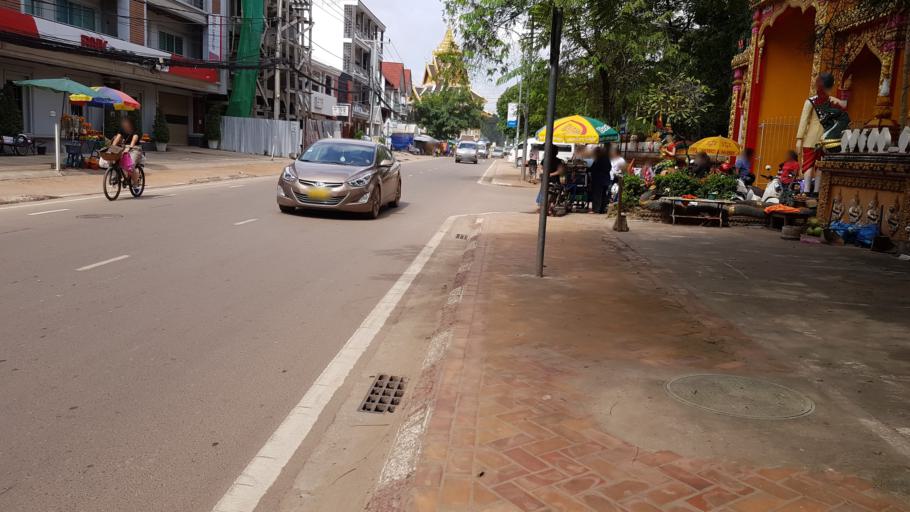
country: LA
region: Vientiane
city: Vientiane
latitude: 17.9576
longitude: 102.6171
